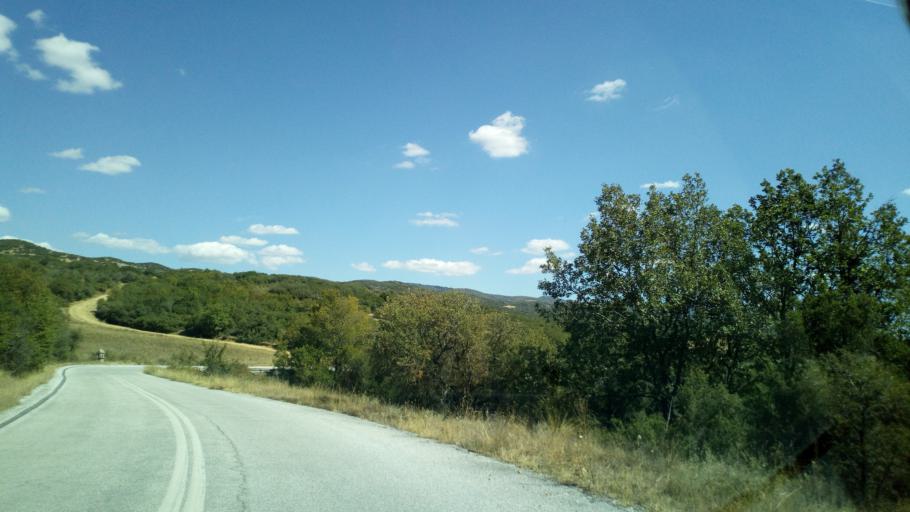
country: GR
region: Central Macedonia
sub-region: Nomos Thessalonikis
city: Kolchikon
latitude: 40.8070
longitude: 23.1906
